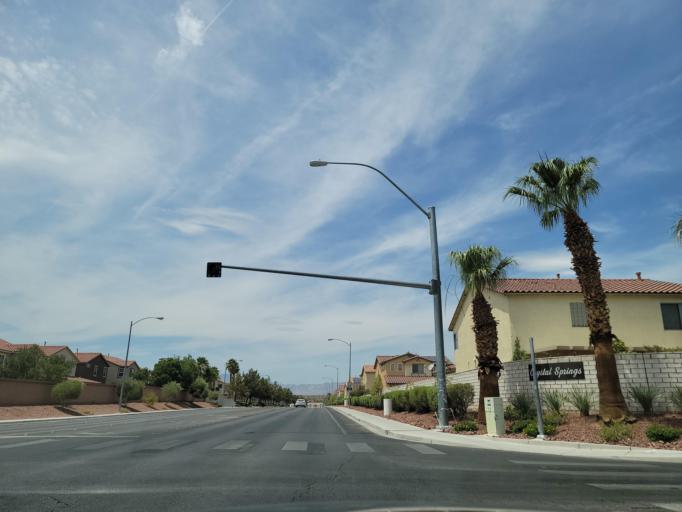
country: US
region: Nevada
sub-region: Clark County
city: Paradise
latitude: 36.0207
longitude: -115.1453
